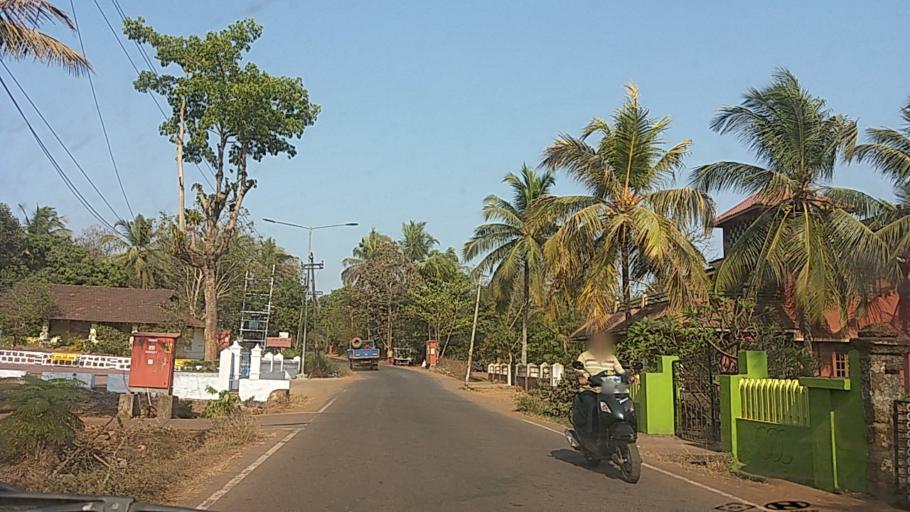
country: IN
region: Goa
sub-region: South Goa
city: Raia
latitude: 15.3075
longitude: 73.9535
